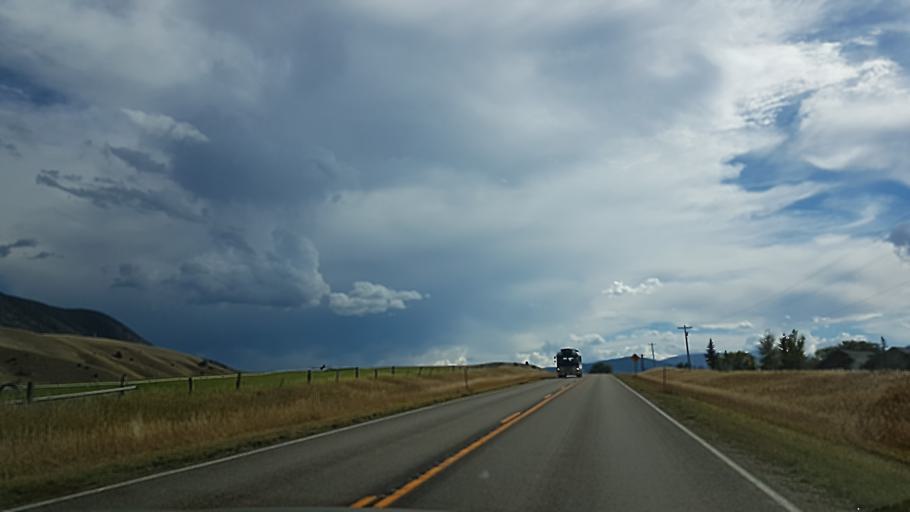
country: US
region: Montana
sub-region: Jefferson County
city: Whitehall
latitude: 45.8418
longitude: -111.9404
